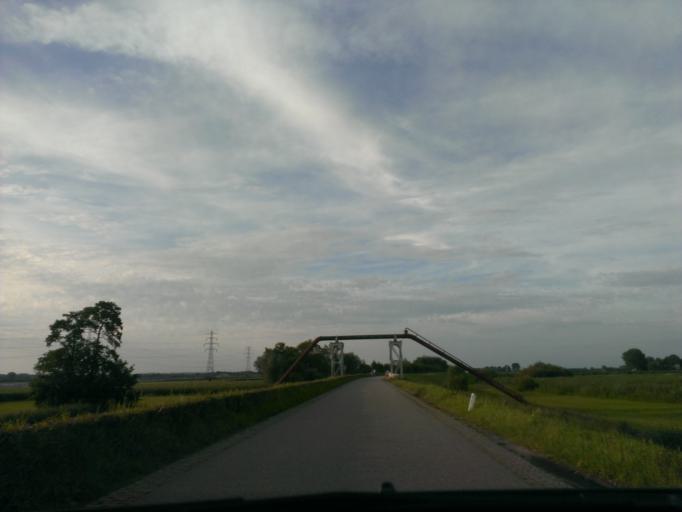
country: NL
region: Gelderland
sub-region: Gemeente Epe
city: Oene
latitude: 52.3701
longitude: 6.0748
